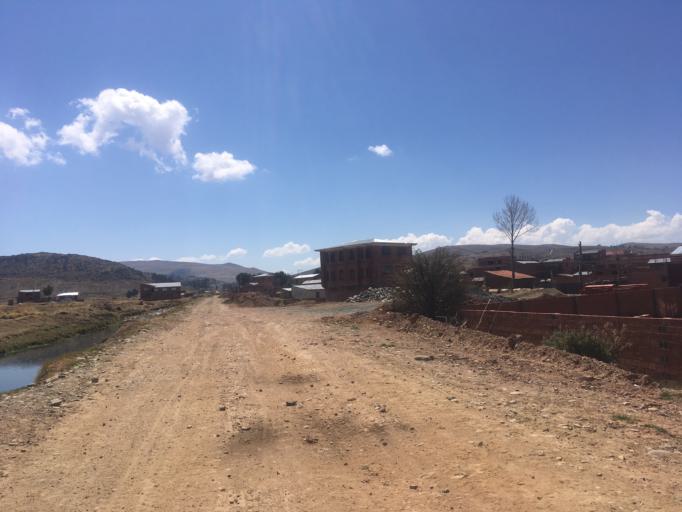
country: BO
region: La Paz
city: Huatajata
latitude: -16.1893
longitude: -68.7458
